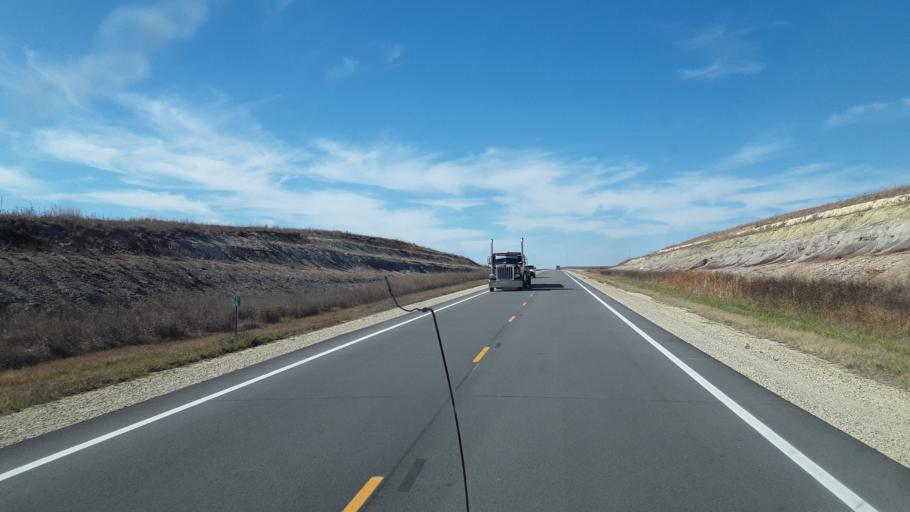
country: US
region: Kansas
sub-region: Chase County
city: Cottonwood Falls
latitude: 38.3627
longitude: -96.6902
